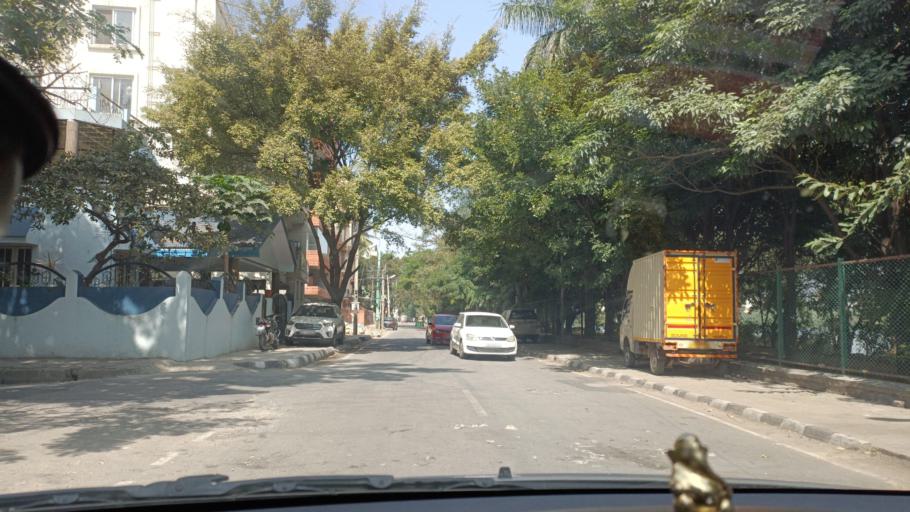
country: IN
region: Karnataka
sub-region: Bangalore Urban
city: Bangalore
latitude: 12.9119
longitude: 77.6158
